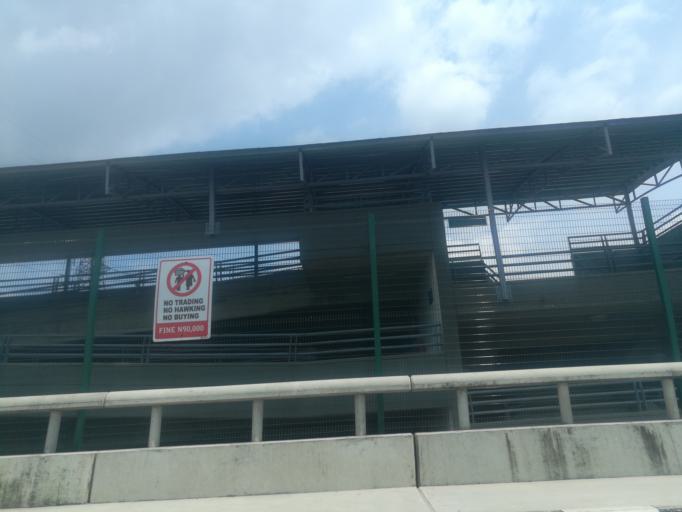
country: NG
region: Lagos
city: Somolu
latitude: 6.5550
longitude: 3.3879
